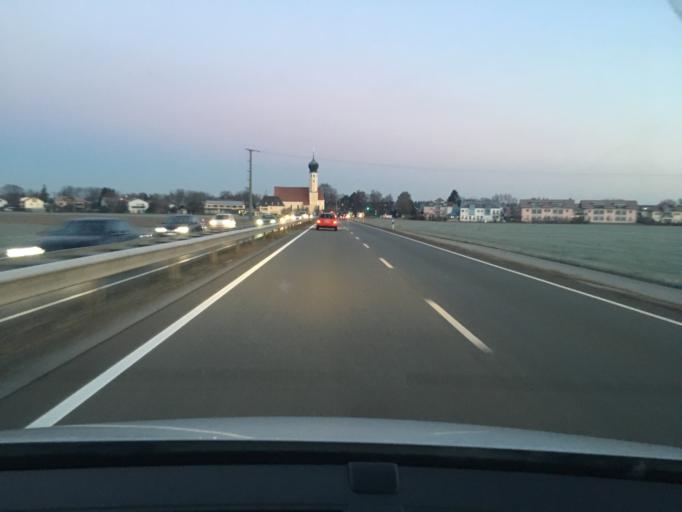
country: DE
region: Bavaria
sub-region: Upper Bavaria
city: Rosenheim
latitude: 47.8324
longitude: 12.1218
